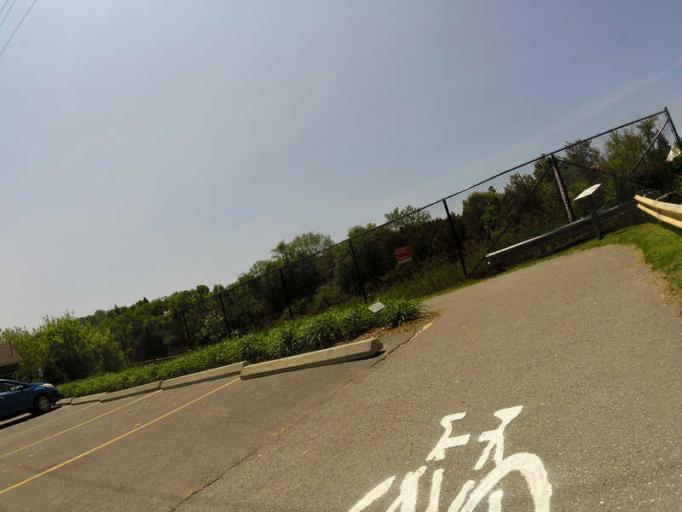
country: CA
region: Ontario
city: Peterborough
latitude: 44.4221
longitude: -78.2734
